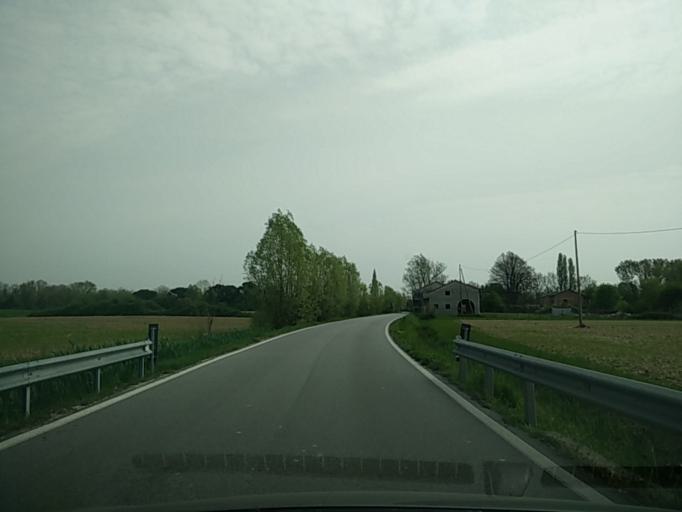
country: IT
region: Veneto
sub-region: Provincia di Venezia
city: Scaltenigo
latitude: 45.4709
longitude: 12.0726
